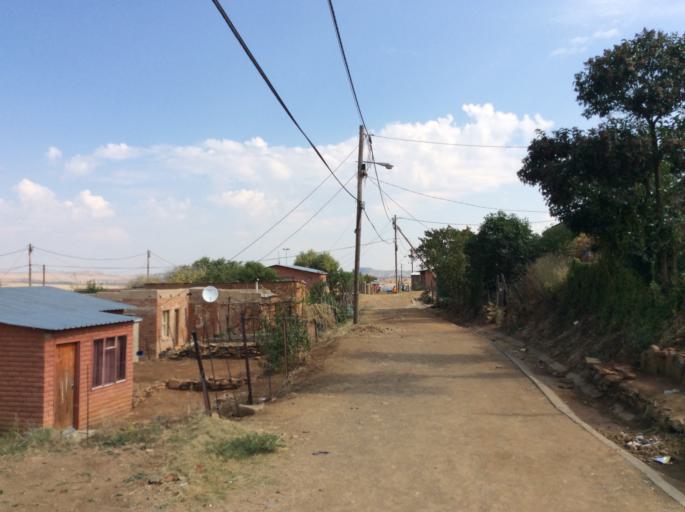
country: LS
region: Mafeteng
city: Mafeteng
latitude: -29.9827
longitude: 27.0062
